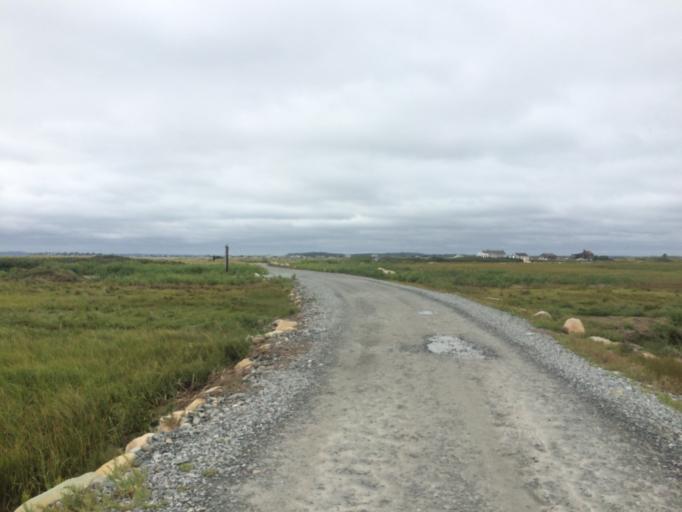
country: US
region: Massachusetts
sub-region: Plymouth County
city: Duxbury
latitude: 42.0050
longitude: -70.6029
